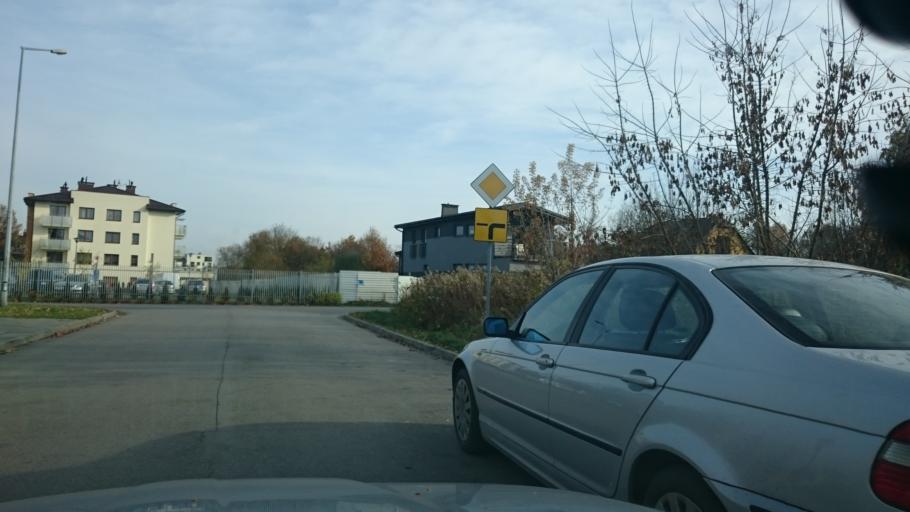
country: PL
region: Lesser Poland Voivodeship
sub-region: Powiat wielicki
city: Czarnochowice
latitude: 50.0194
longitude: 20.0508
